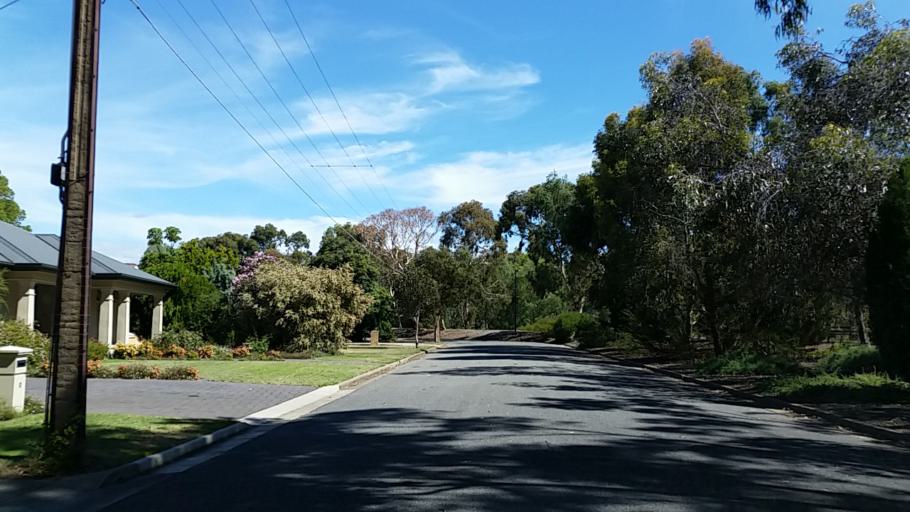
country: AU
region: South Australia
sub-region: Charles Sturt
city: Seaton
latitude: -34.9211
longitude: 138.5209
